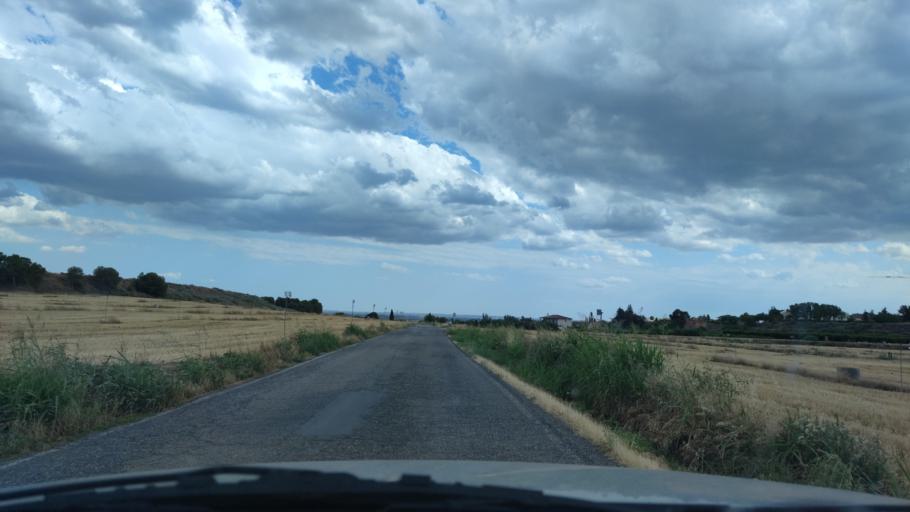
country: ES
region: Catalonia
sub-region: Provincia de Lleida
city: Lleida
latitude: 41.6066
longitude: 0.5849
